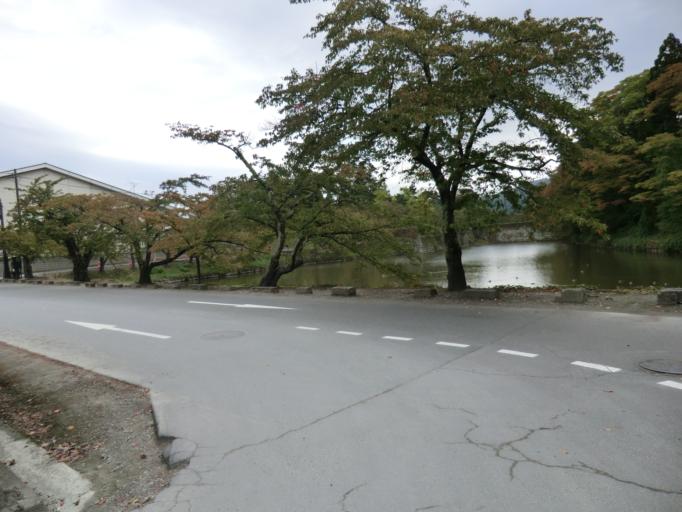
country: JP
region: Fukushima
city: Kitakata
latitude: 37.4884
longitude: 139.9277
